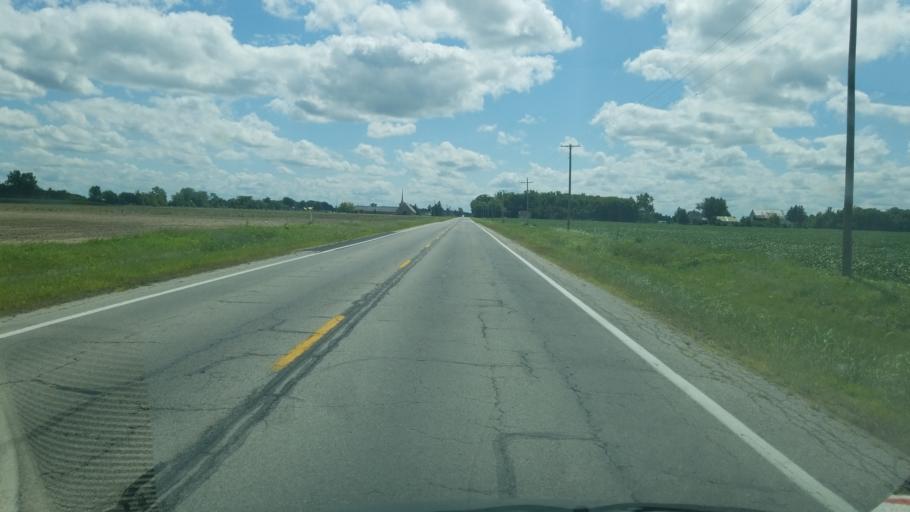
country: US
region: Ohio
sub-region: Henry County
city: Holgate
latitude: 41.3023
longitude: -84.1177
